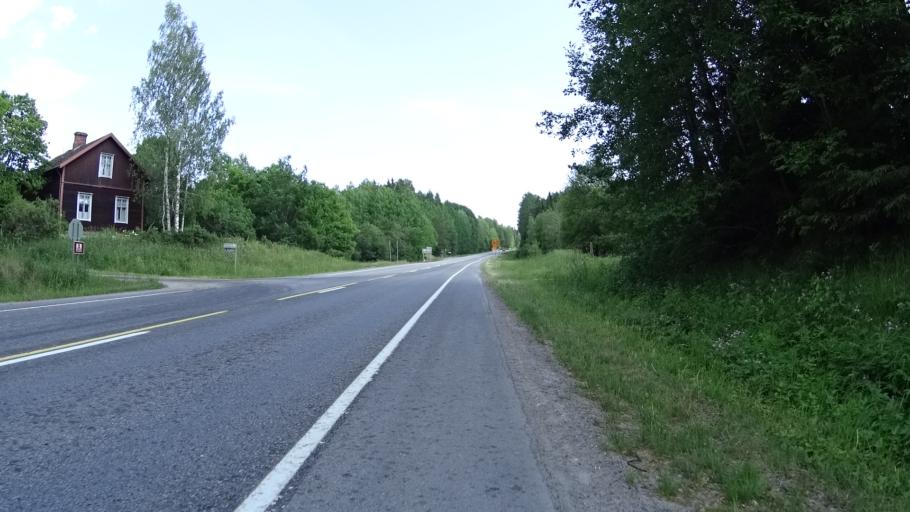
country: FI
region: Uusimaa
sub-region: Raaseporin
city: Karis
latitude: 60.0941
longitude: 23.6319
